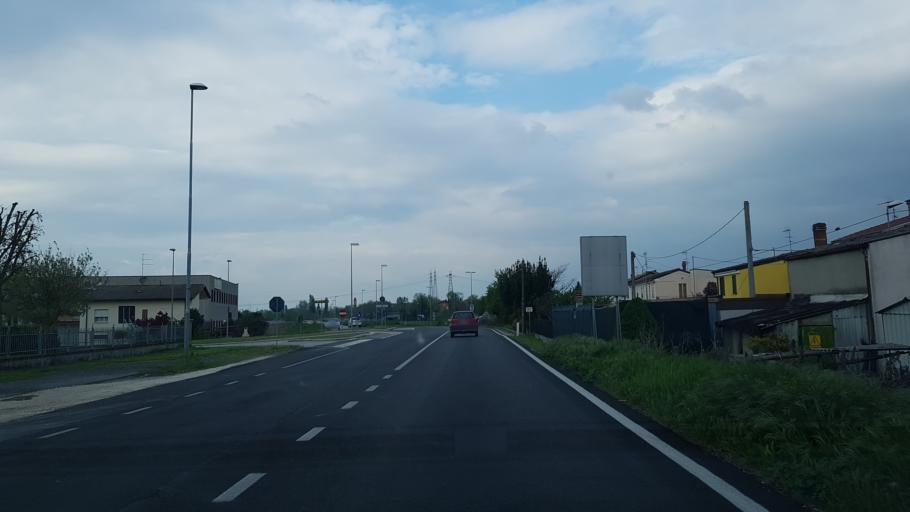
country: IT
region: Lombardy
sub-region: Provincia di Mantova
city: Ostiglia
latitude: 45.0755
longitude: 11.1353
